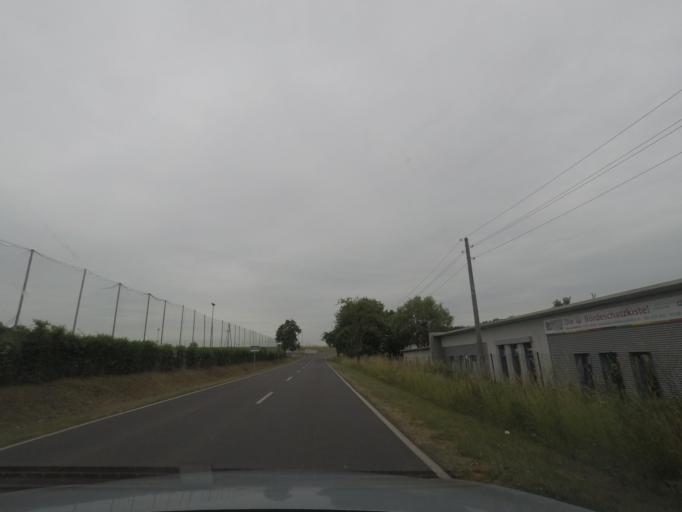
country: DE
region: Saxony-Anhalt
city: Seehausen
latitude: 52.0955
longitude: 11.2923
